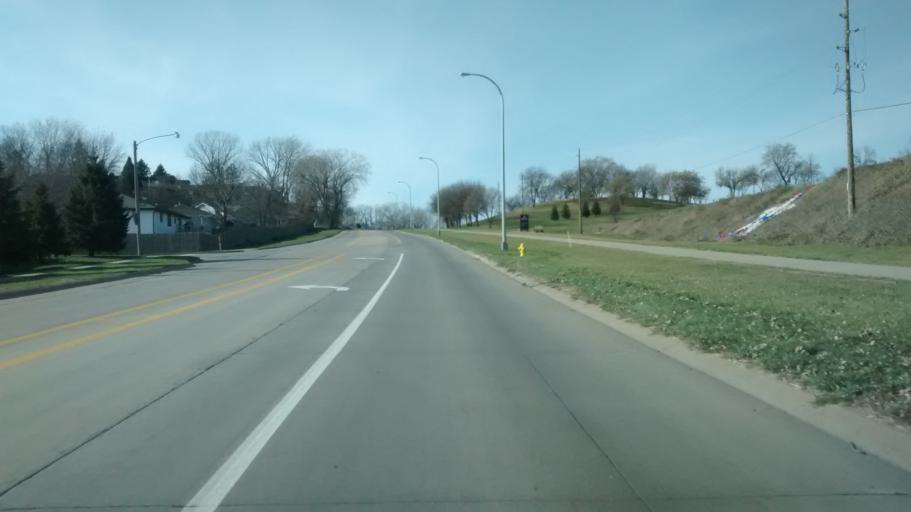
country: US
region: Iowa
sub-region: Woodbury County
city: Sioux City
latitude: 42.5411
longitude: -96.3889
